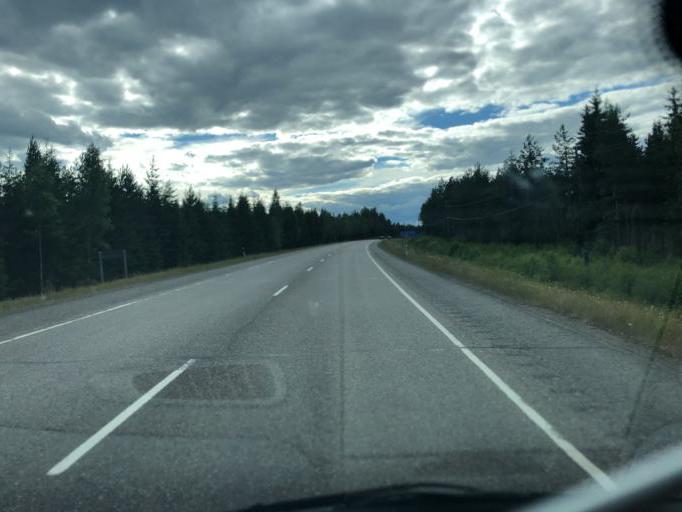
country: FI
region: Kymenlaakso
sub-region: Kouvola
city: Kouvola
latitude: 60.8659
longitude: 26.5701
